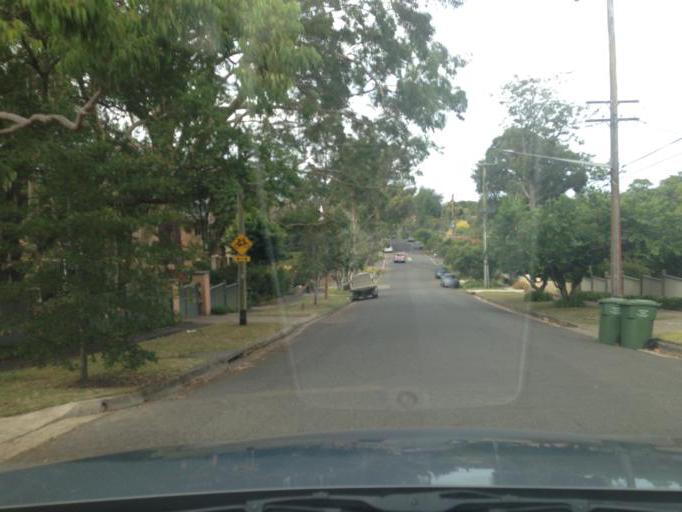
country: AU
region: New South Wales
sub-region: Ku-ring-gai
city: Killara
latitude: -33.7675
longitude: 151.1670
